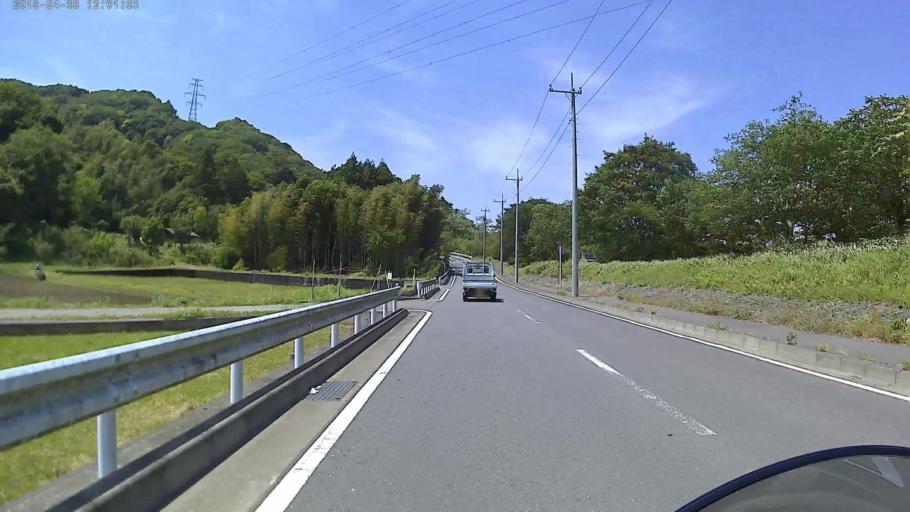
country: JP
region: Kanagawa
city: Zama
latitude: 35.5204
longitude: 139.3228
